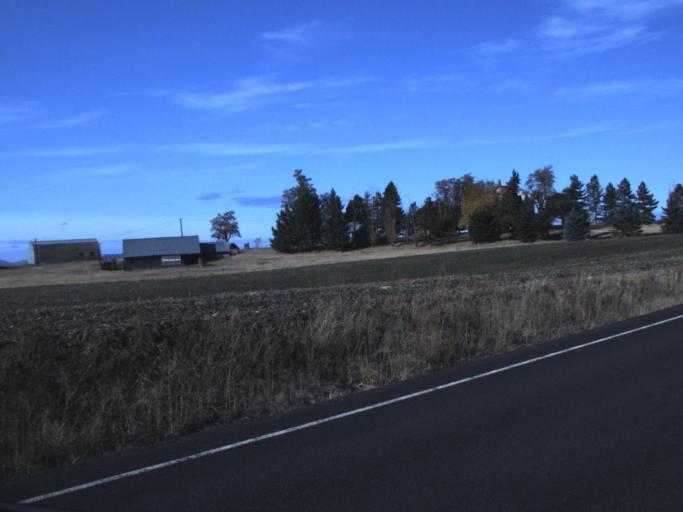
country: US
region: Washington
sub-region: Lincoln County
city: Davenport
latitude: 47.7902
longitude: -118.1737
